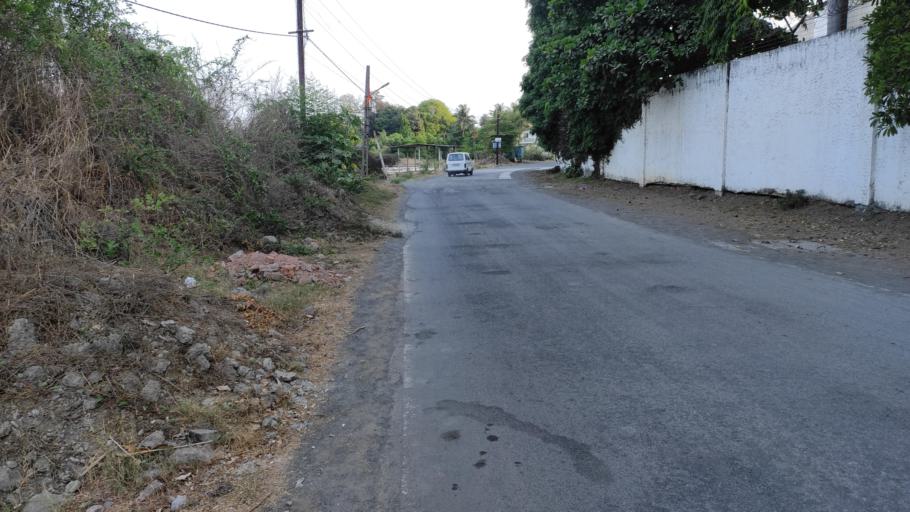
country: IN
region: Daman and Diu
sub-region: Daman District
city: Daman
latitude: 20.4129
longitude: 72.8576
